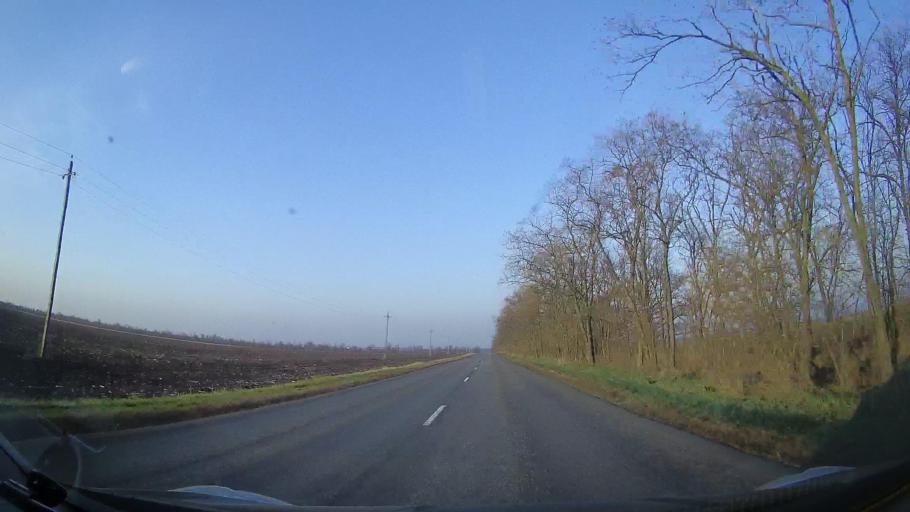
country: RU
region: Rostov
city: Ol'ginskaya
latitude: 47.0929
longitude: 39.9776
